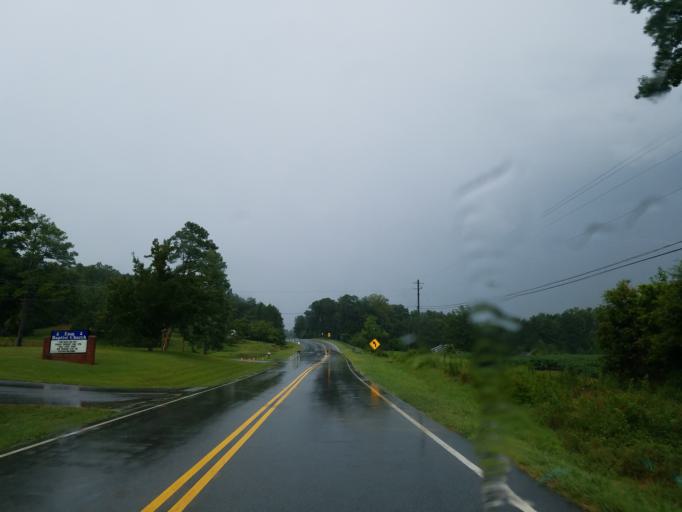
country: US
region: Georgia
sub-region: Floyd County
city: Shannon
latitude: 34.3677
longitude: -85.0803
